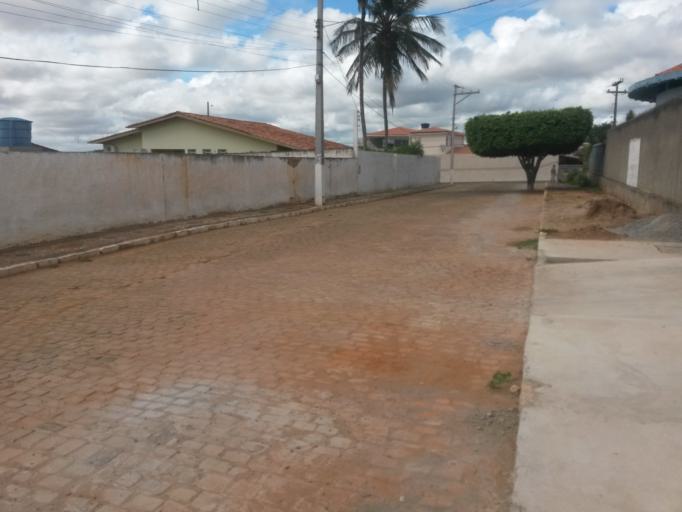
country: BR
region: Bahia
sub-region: Mairi
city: Mairi
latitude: -11.7058
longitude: -40.1502
